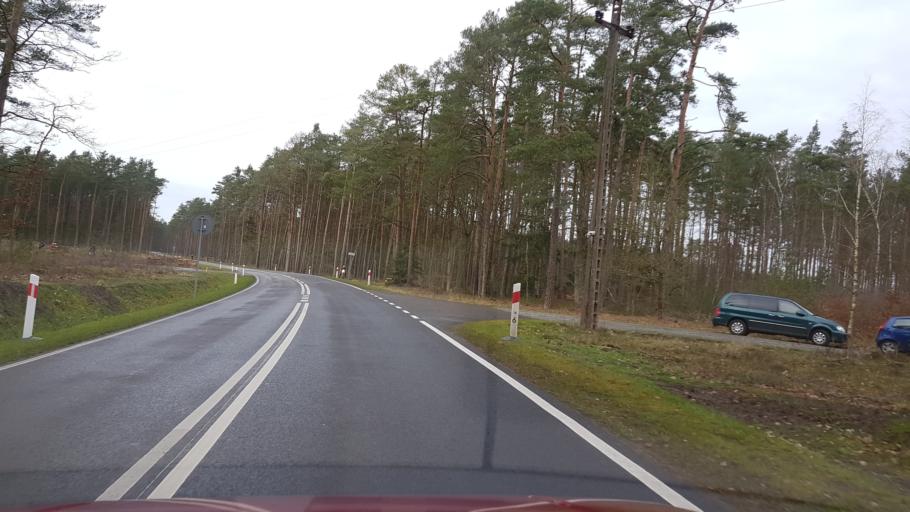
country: PL
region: West Pomeranian Voivodeship
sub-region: Powiat policki
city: Police
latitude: 53.6550
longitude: 14.4788
